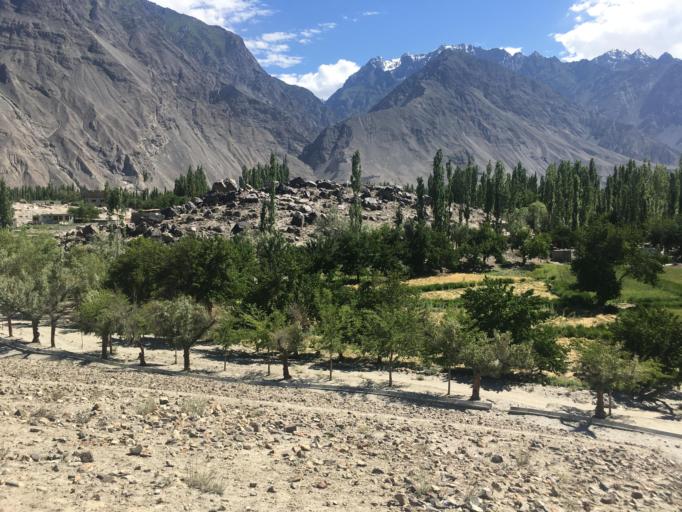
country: PK
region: Gilgit-Baltistan
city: Skardu
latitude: 35.2908
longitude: 75.6110
